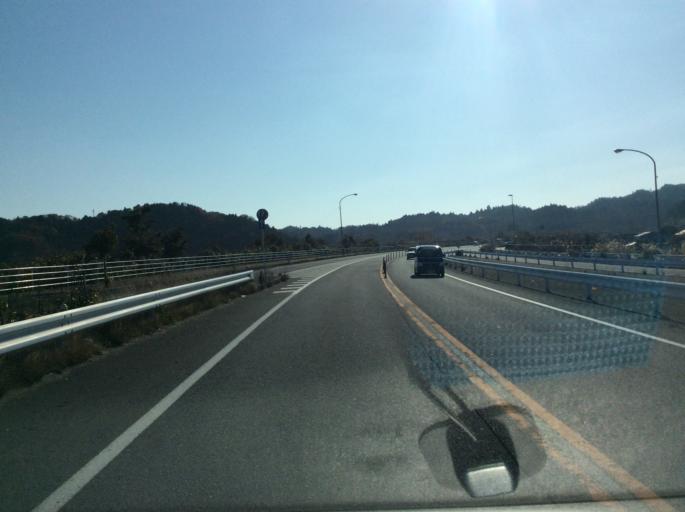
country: JP
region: Fukushima
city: Iwaki
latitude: 37.0540
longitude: 140.9438
